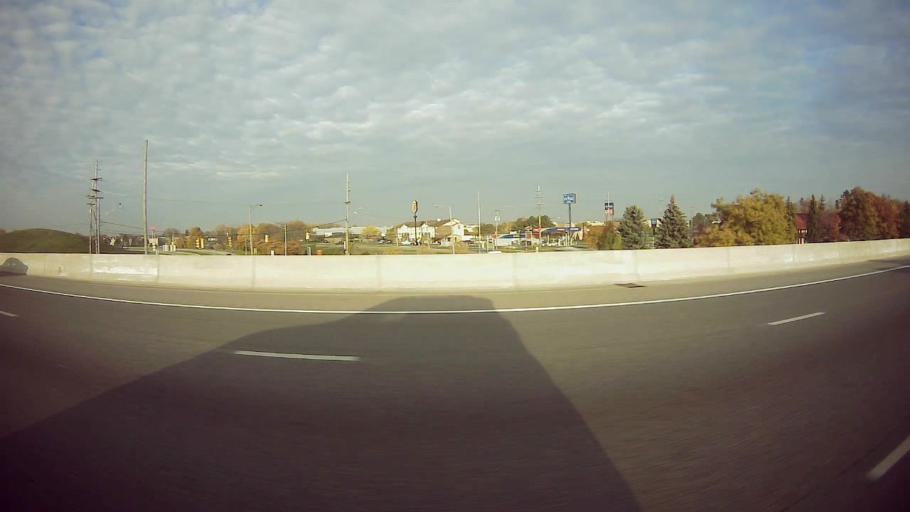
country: US
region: Michigan
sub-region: Macomb County
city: Saint Clair Shores
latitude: 42.5267
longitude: -82.9100
